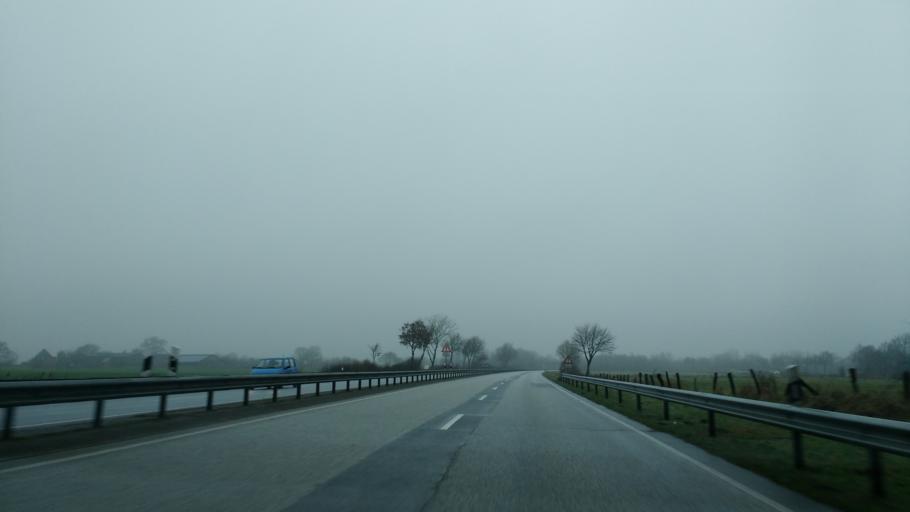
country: DE
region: Schleswig-Holstein
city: Jevenstedt
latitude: 54.2527
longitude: 9.6672
